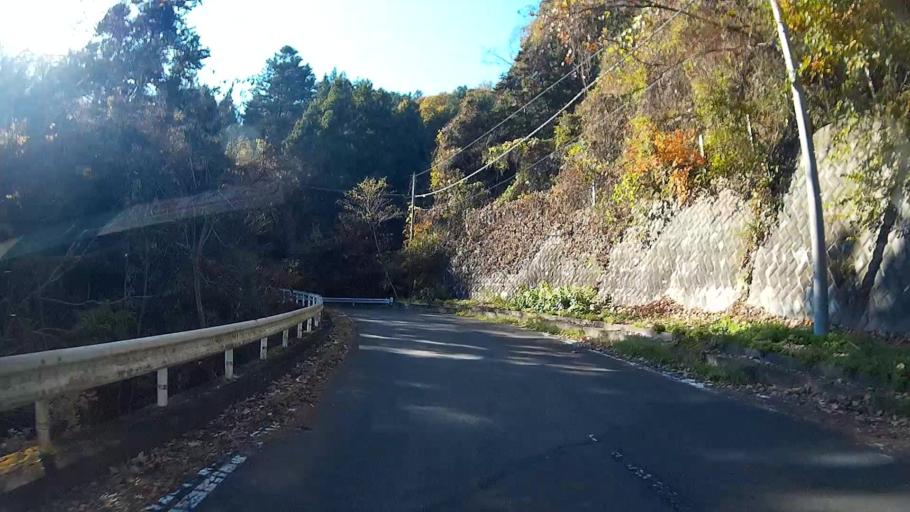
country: JP
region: Yamanashi
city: Uenohara
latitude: 35.5910
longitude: 139.1283
